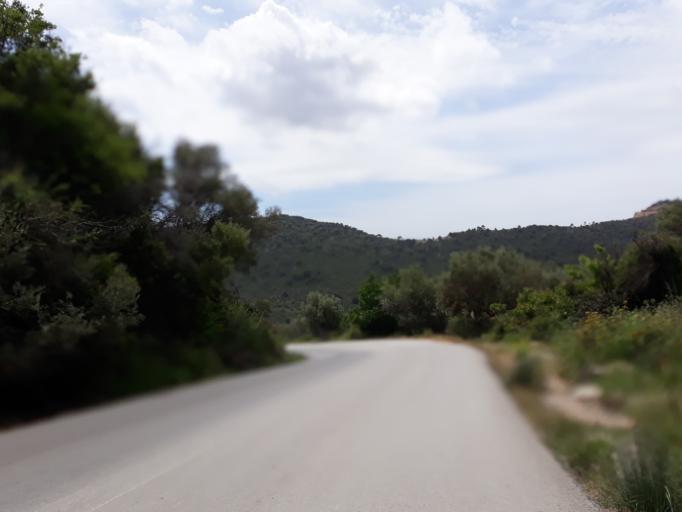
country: GR
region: Attica
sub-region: Nomarchia Dytikis Attikis
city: Magoula
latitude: 38.1468
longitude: 23.5248
